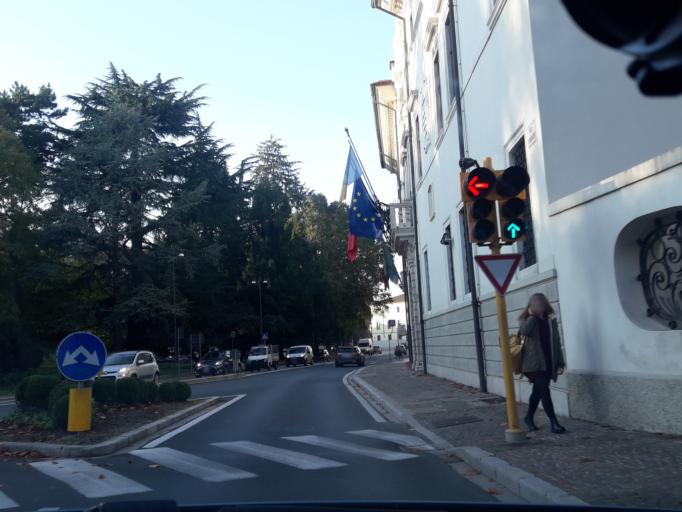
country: IT
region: Friuli Venezia Giulia
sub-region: Provincia di Udine
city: Udine
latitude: 46.0630
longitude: 13.2407
